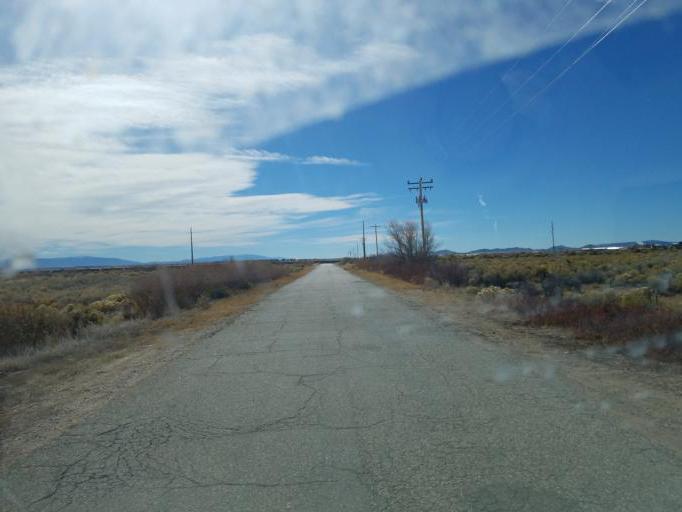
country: US
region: Colorado
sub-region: Costilla County
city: San Luis
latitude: 37.4376
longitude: -105.5230
